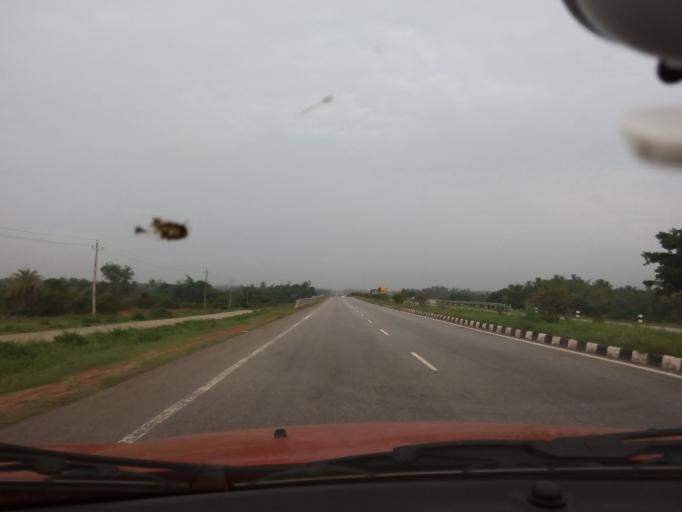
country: IN
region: Karnataka
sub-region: Tumkur
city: Kunigal
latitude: 13.0050
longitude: 77.0086
